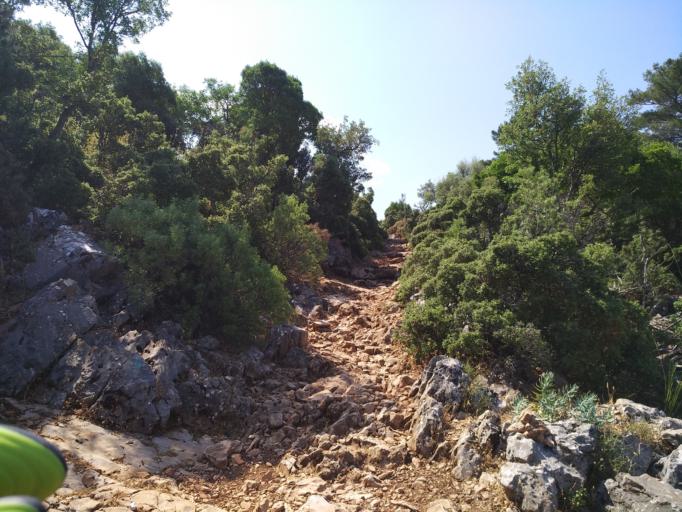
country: TR
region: Mugla
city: OEluedeniz
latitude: 36.5313
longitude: 29.1414
